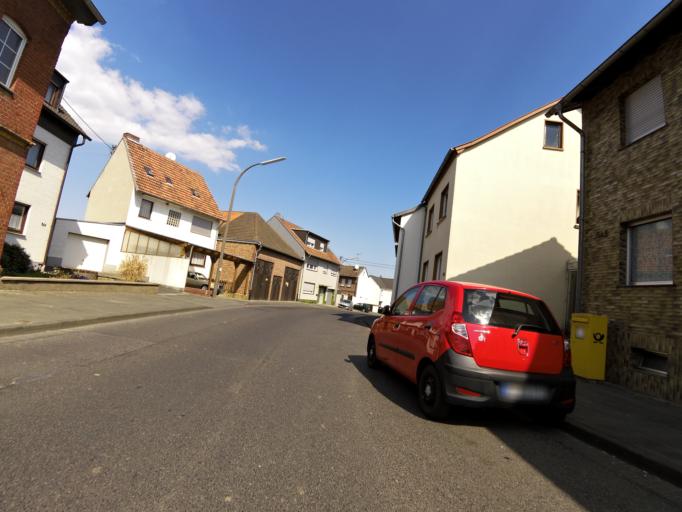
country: DE
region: North Rhine-Westphalia
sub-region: Regierungsbezirk Koln
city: Alfter
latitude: 50.6788
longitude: 7.0169
